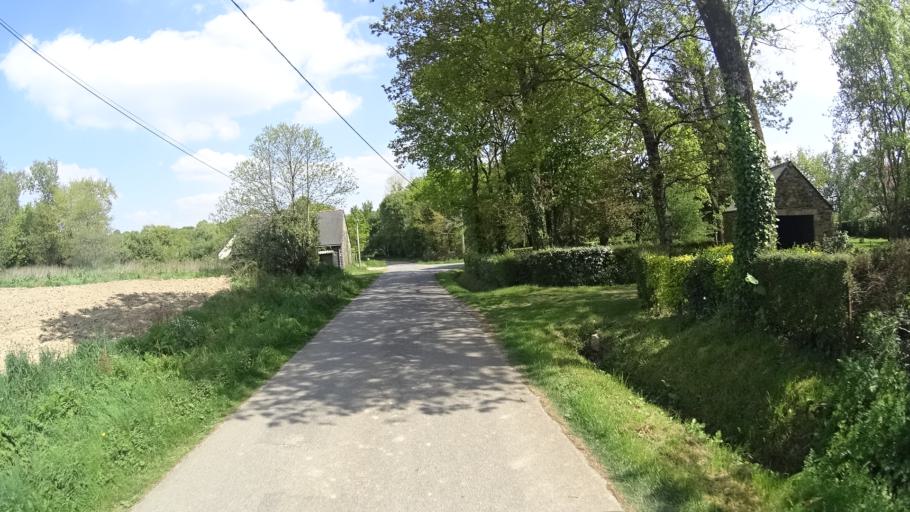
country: FR
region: Brittany
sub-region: Departement du Morbihan
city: Allaire
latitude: 47.5993
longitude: -2.1760
